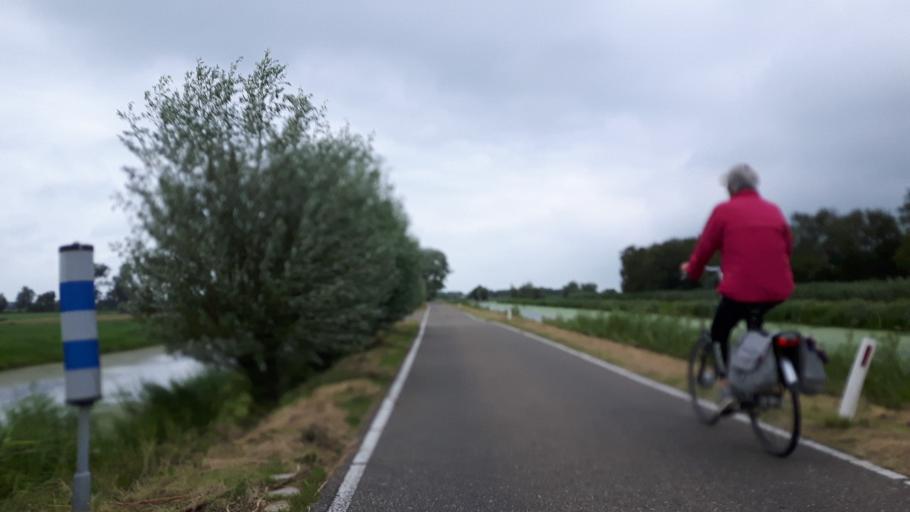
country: NL
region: South Holland
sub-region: Bodegraven-Reeuwijk
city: Bodegraven
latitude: 52.1173
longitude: 4.7501
